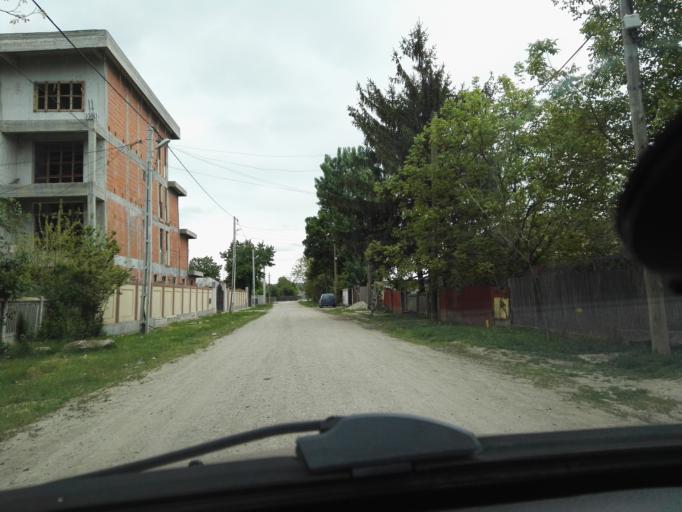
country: RO
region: Olt
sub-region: Comuna Draganesti-Olt
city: Draganesti-Olt
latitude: 44.1670
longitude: 24.5207
